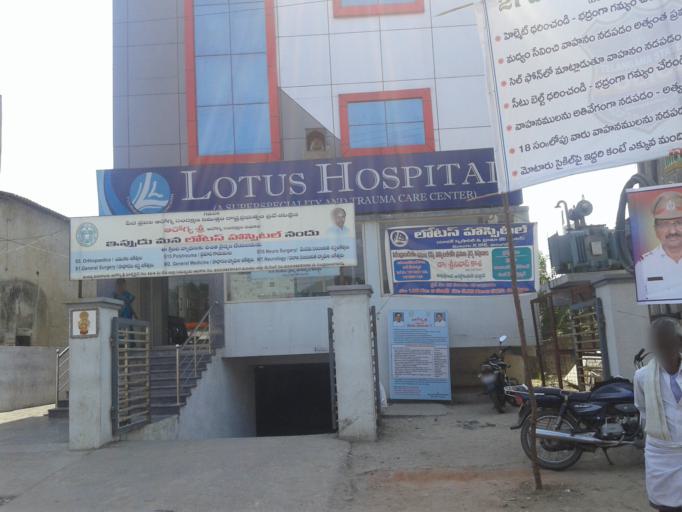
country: IN
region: Telangana
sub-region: Warangal
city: Warangal
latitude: 18.0001
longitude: 79.5832
